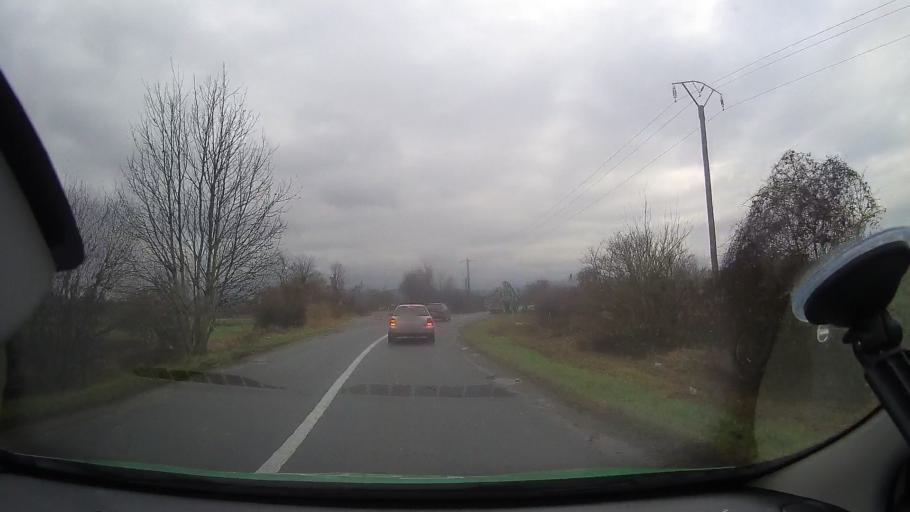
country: RO
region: Arad
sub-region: Comuna Sebis
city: Sebis
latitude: 46.3515
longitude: 22.1303
